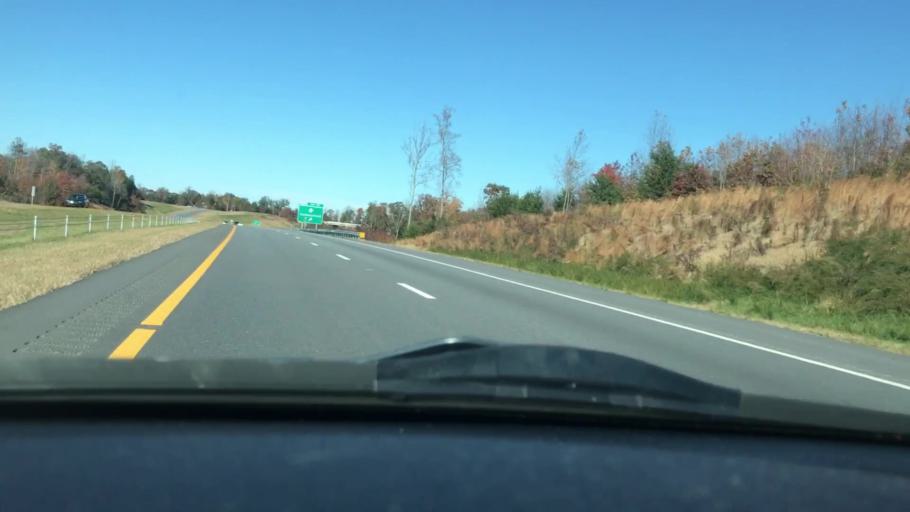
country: US
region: North Carolina
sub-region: Guilford County
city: Summerfield
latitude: 36.1949
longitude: -79.9289
